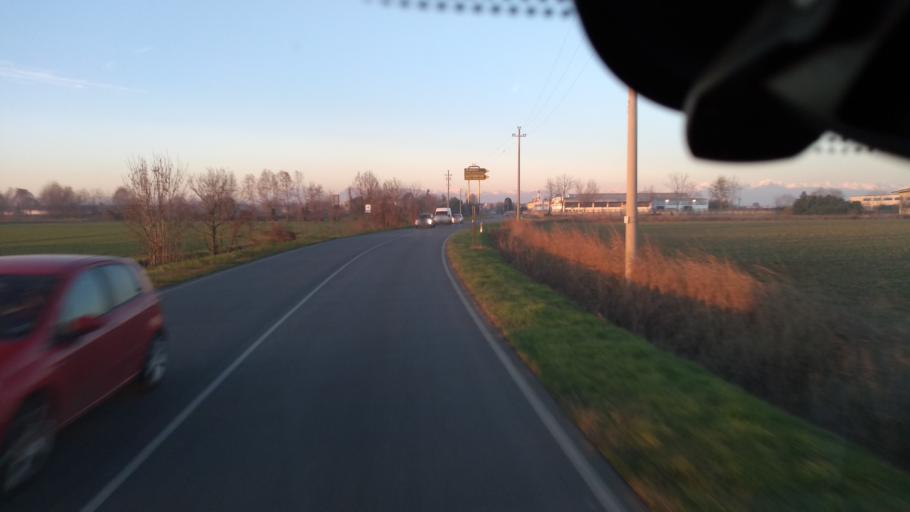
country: IT
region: Lombardy
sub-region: Provincia di Bergamo
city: Calvenzano
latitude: 45.4839
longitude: 9.6012
